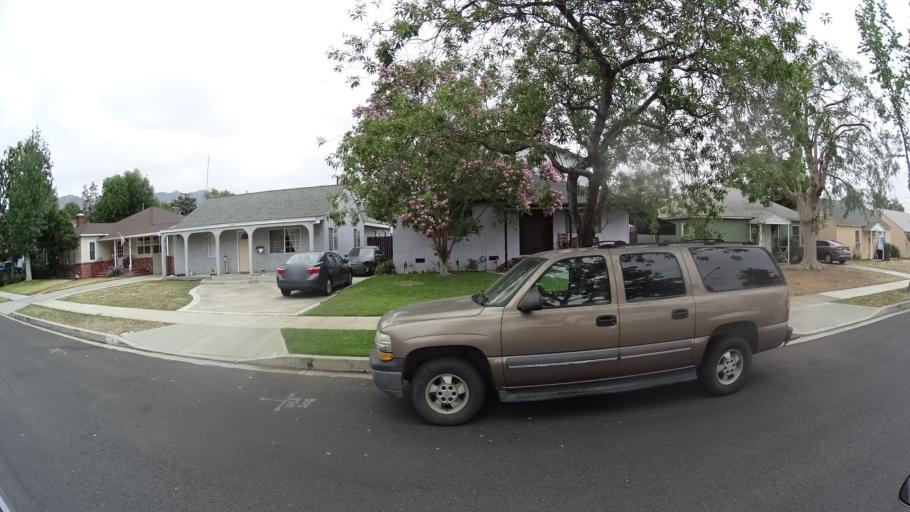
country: US
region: California
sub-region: Los Angeles County
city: Burbank
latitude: 34.1857
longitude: -118.3284
